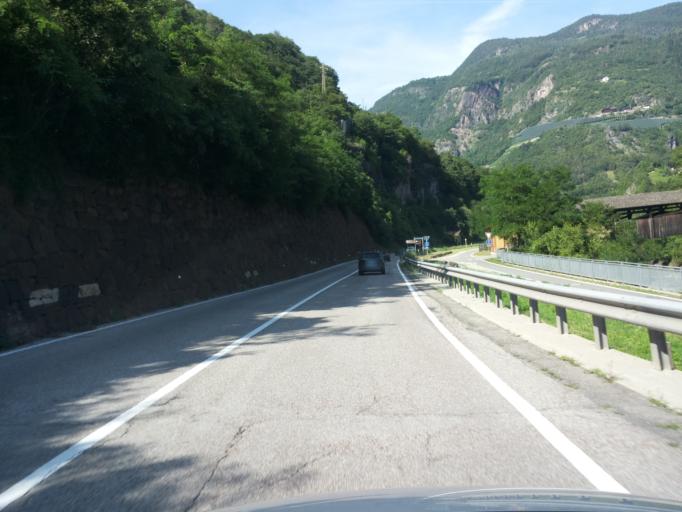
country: IT
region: Trentino-Alto Adige
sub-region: Bolzano
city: Ponte Gardena
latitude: 46.5642
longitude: 11.5147
